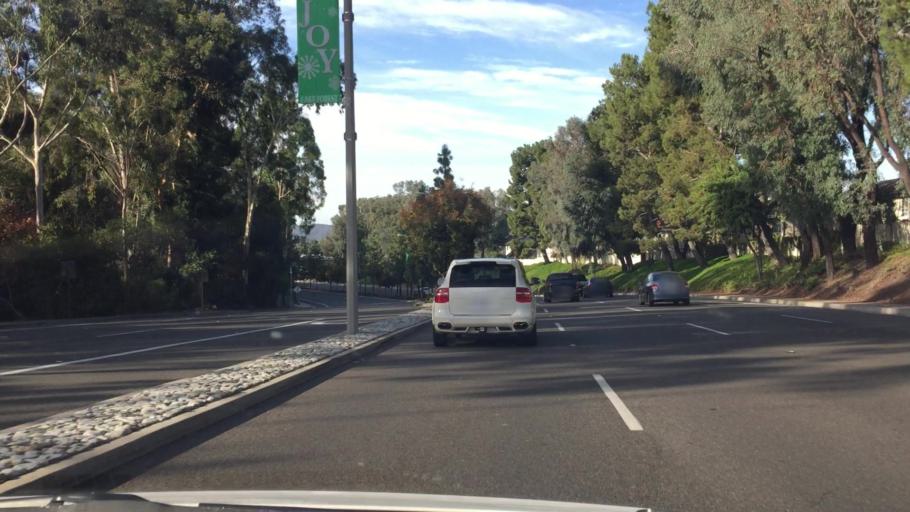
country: US
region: California
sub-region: Orange County
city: Lake Forest
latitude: 33.6404
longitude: -117.7041
